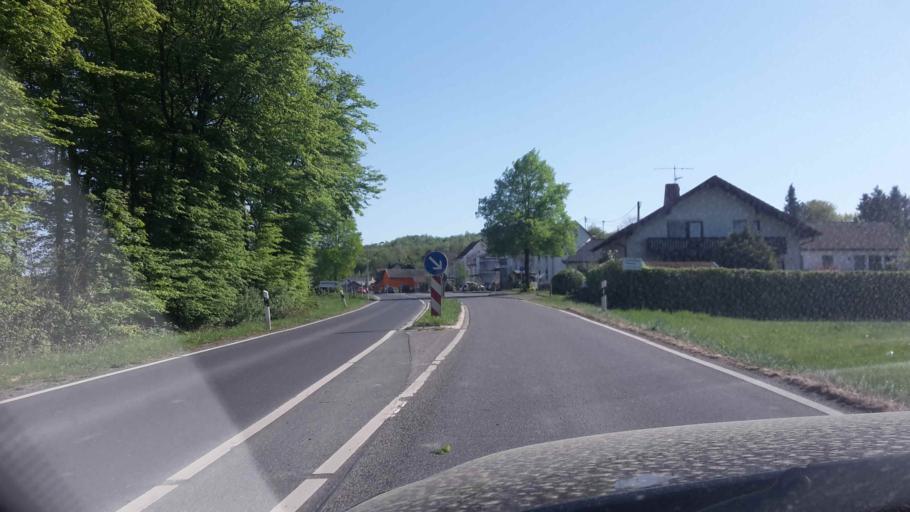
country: DE
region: Rheinland-Pfalz
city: Windhagen
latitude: 50.7003
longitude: 7.3187
